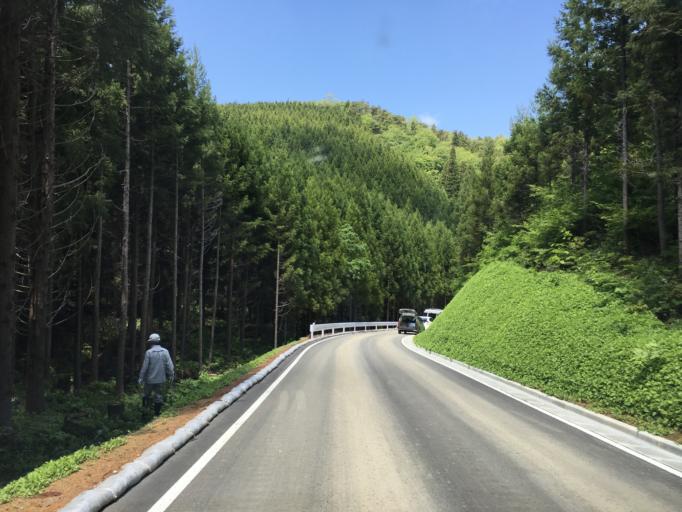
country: JP
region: Miyagi
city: Wakuya
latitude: 38.6904
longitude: 141.3482
